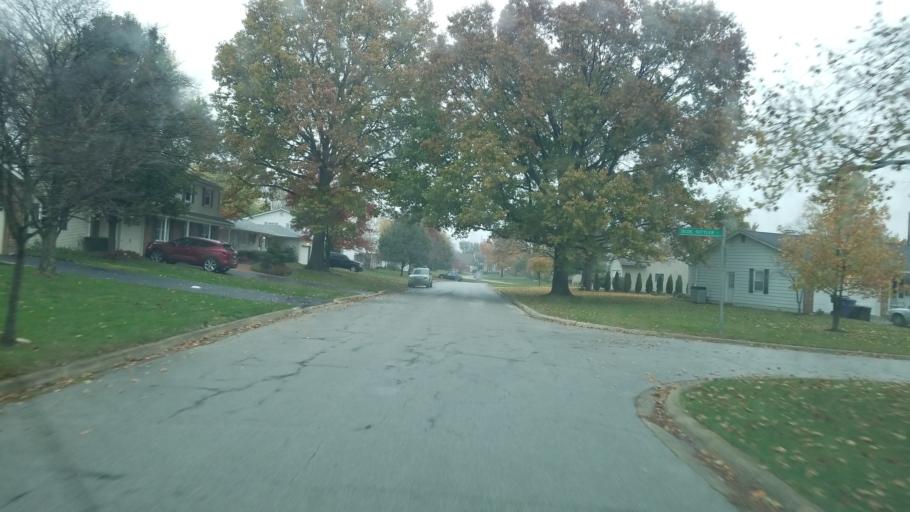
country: US
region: Ohio
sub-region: Franklin County
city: Worthington
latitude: 40.0494
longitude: -83.0419
